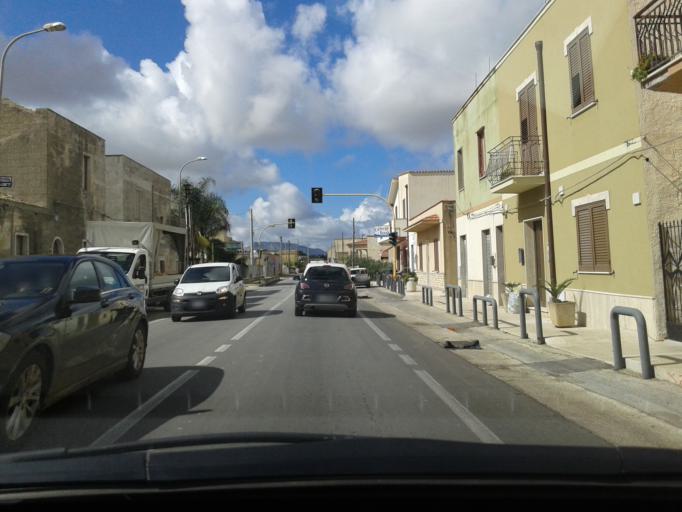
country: IT
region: Sicily
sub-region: Trapani
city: Custonaci
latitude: 38.0804
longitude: 12.7146
